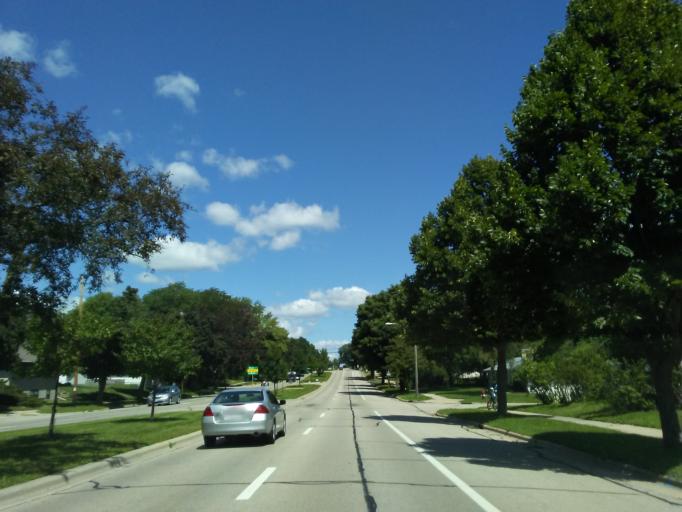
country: US
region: Wisconsin
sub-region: Dane County
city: Shorewood Hills
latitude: 43.0471
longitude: -89.4510
